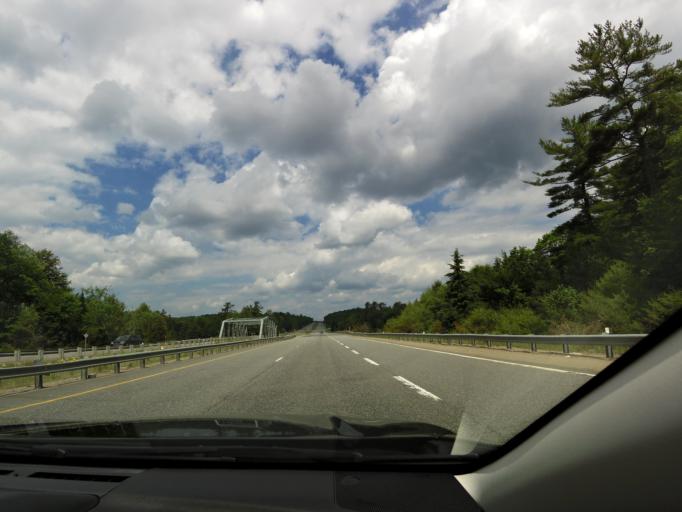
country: CA
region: Ontario
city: Bracebridge
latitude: 45.0872
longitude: -79.2989
